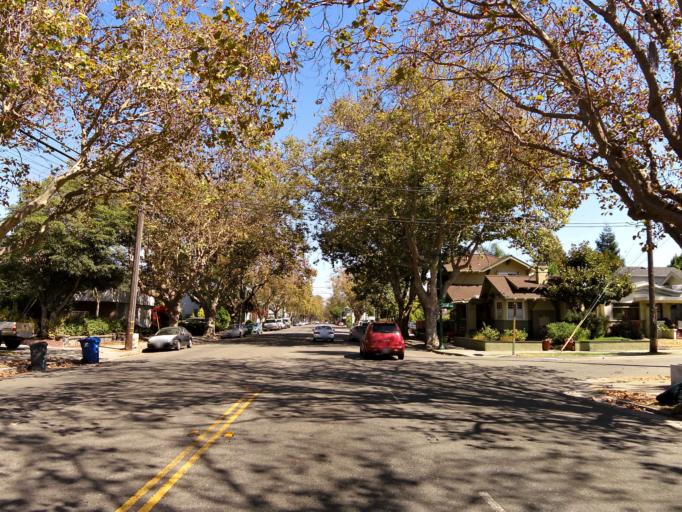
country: US
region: California
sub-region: Alameda County
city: Alameda
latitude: 37.7713
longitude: -122.2722
